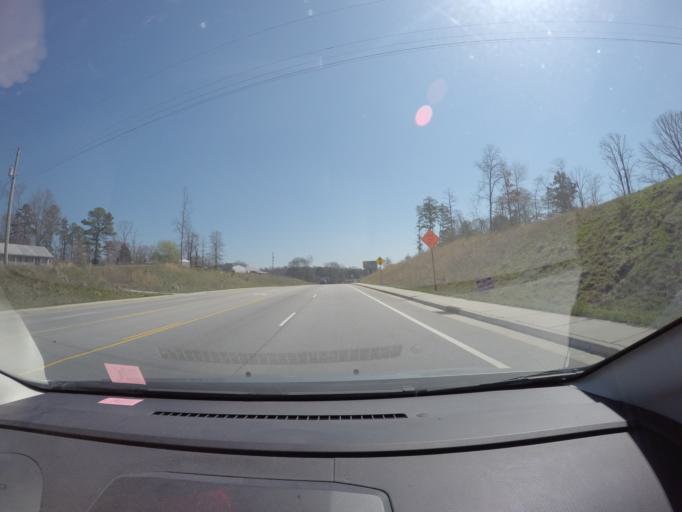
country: US
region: Tennessee
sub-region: Hamilton County
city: Harrison
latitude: 35.0705
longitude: -85.1043
